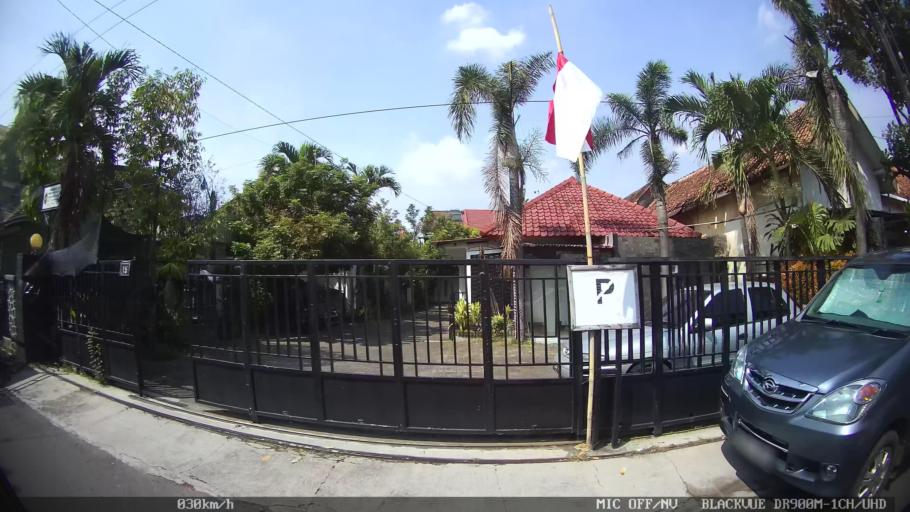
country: ID
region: Daerah Istimewa Yogyakarta
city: Yogyakarta
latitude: -7.7854
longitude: 110.3658
